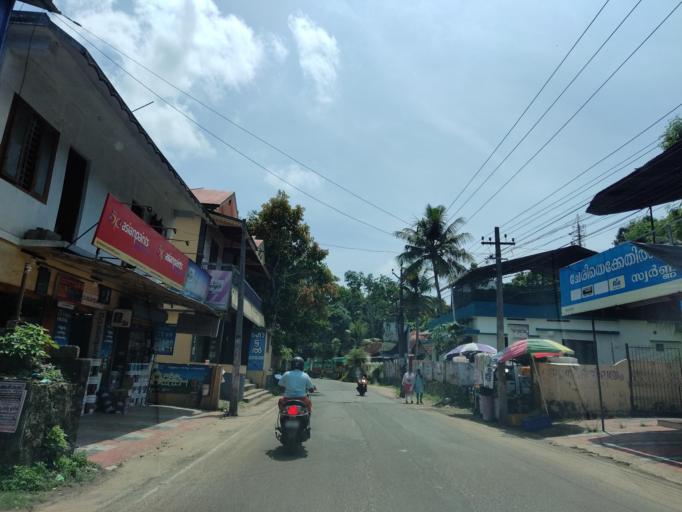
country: IN
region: Kerala
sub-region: Alappuzha
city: Chengannur
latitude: 9.3098
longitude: 76.5660
